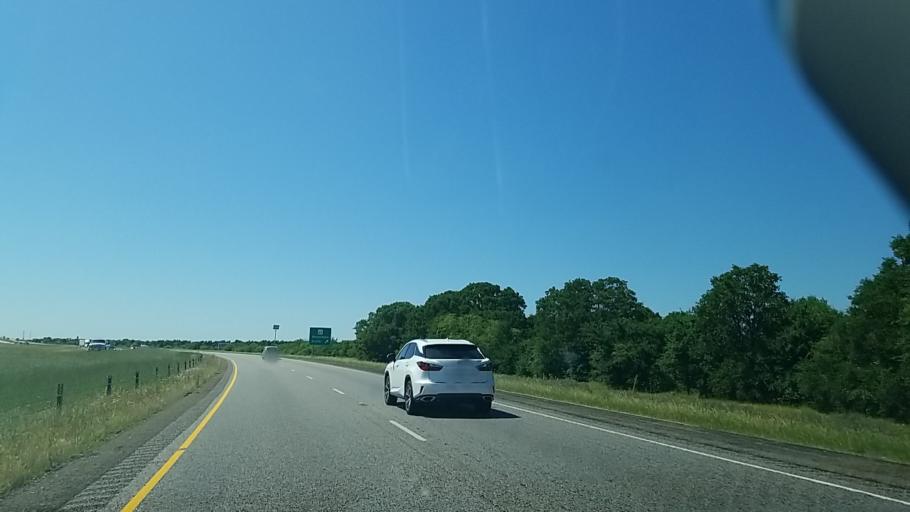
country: US
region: Texas
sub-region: Freestone County
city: Wortham
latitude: 31.8593
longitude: -96.3093
